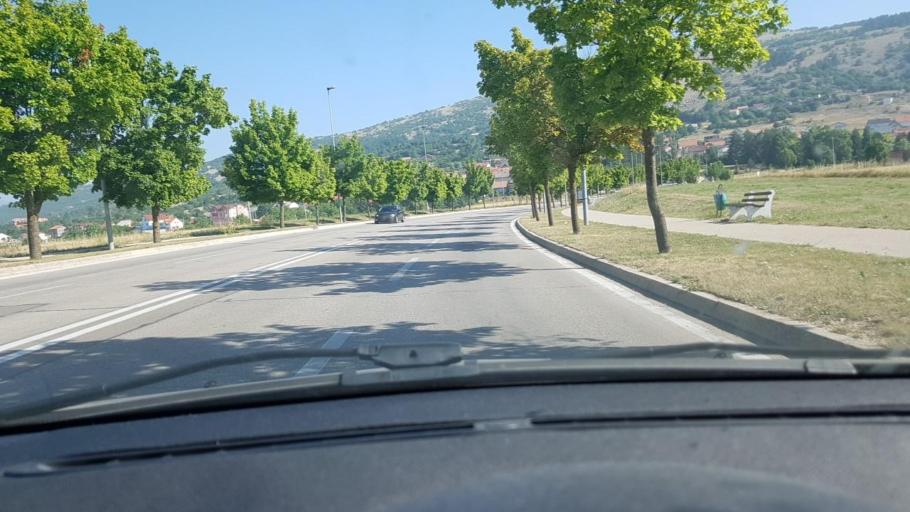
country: BA
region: Federation of Bosnia and Herzegovina
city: Livno
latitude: 43.8257
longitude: 16.9966
